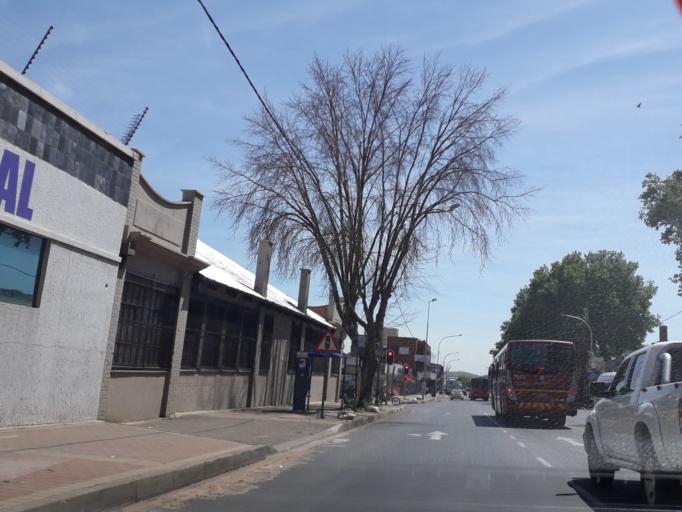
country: ZA
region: Gauteng
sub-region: City of Johannesburg Metropolitan Municipality
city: Johannesburg
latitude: -26.2000
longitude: 28.0650
